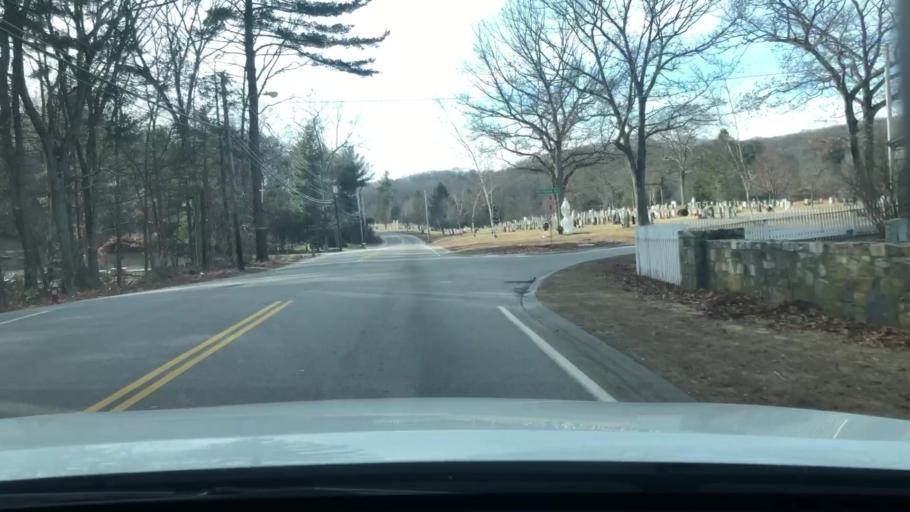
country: US
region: Massachusetts
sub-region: Worcester County
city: Grafton
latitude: 42.2041
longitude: -71.6982
